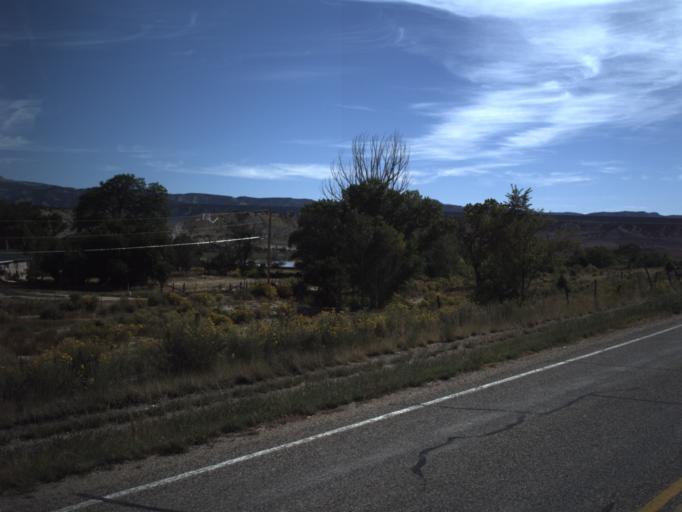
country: US
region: Utah
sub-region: Garfield County
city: Panguitch
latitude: 37.6218
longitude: -112.0809
